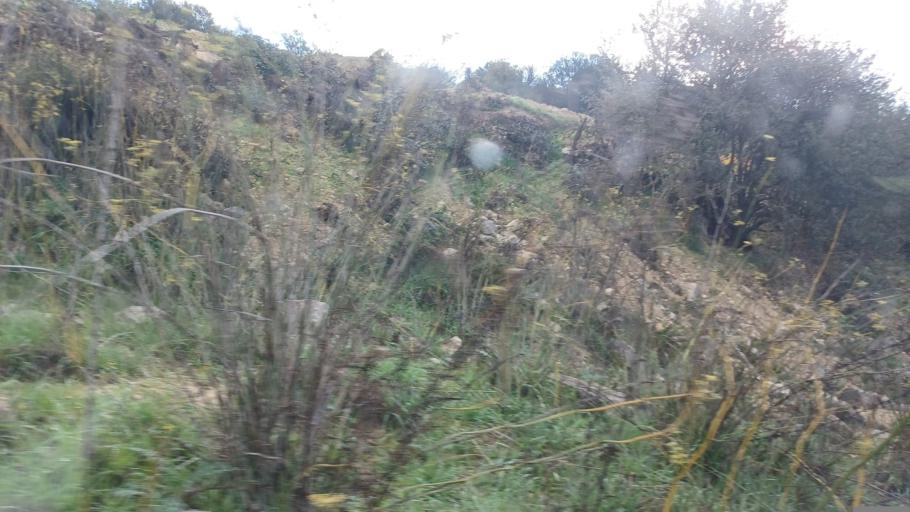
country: CY
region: Pafos
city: Mesogi
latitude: 34.8412
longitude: 32.5457
